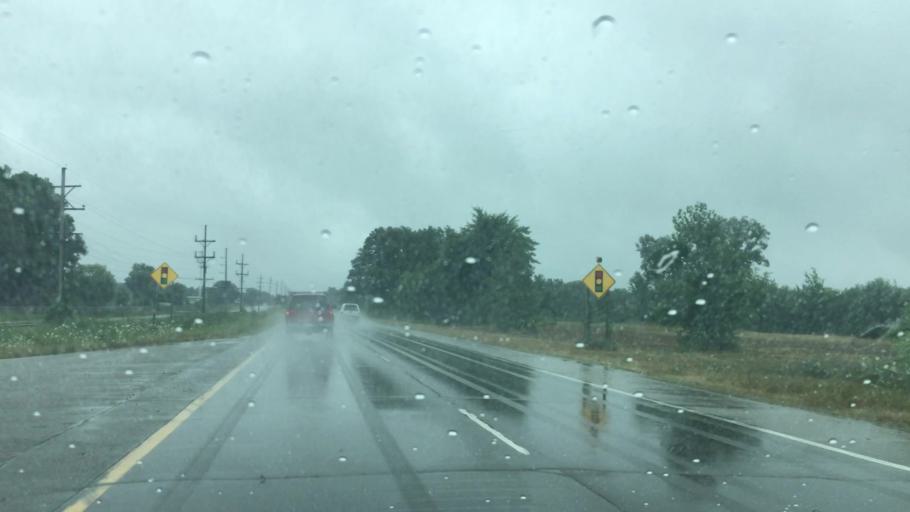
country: US
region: Michigan
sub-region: Ottawa County
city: Jenison
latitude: 42.8929
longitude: -85.8190
